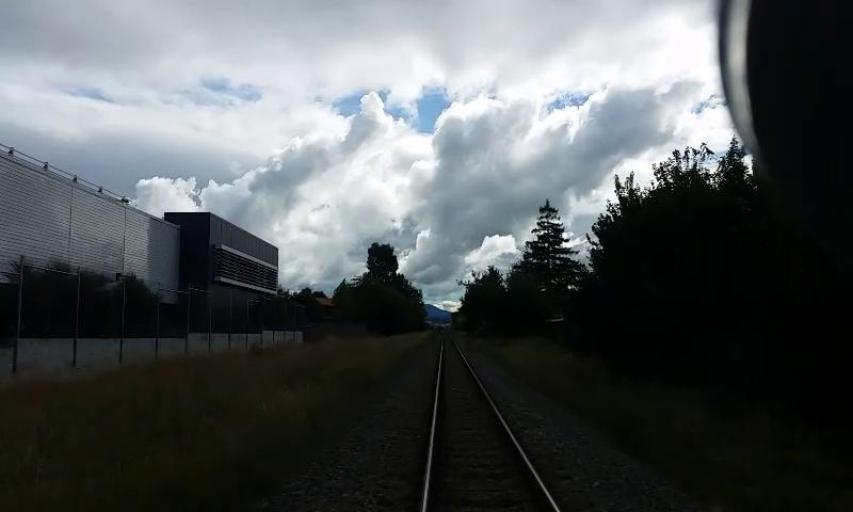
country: NZ
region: Canterbury
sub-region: Waimakariri District
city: Woodend
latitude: -43.3075
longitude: 172.5994
